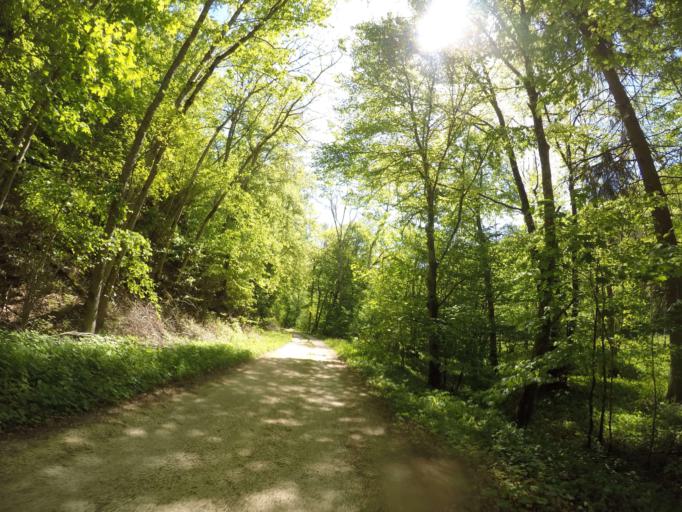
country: DE
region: Baden-Wuerttemberg
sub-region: Tuebingen Region
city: Blaubeuren
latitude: 48.4013
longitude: 9.7538
